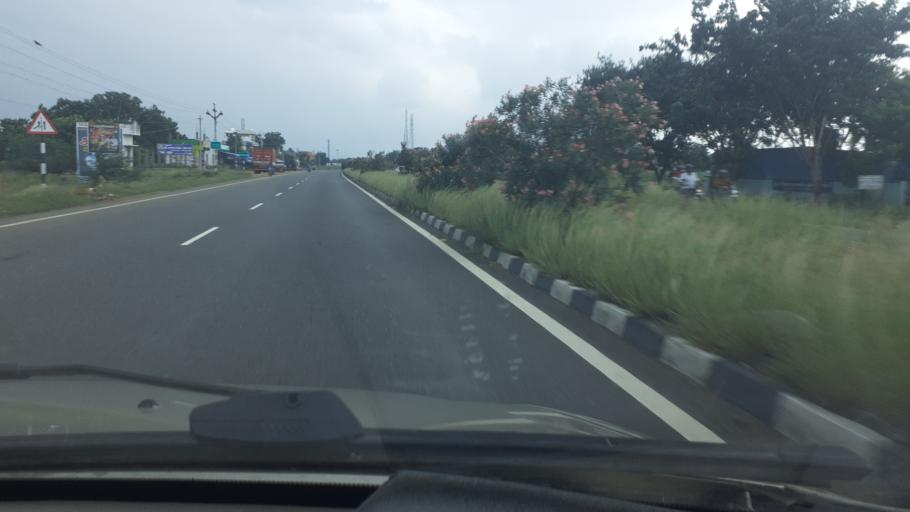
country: IN
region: Tamil Nadu
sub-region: Madurai
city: Kallupatti
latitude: 9.7032
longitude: 77.9731
